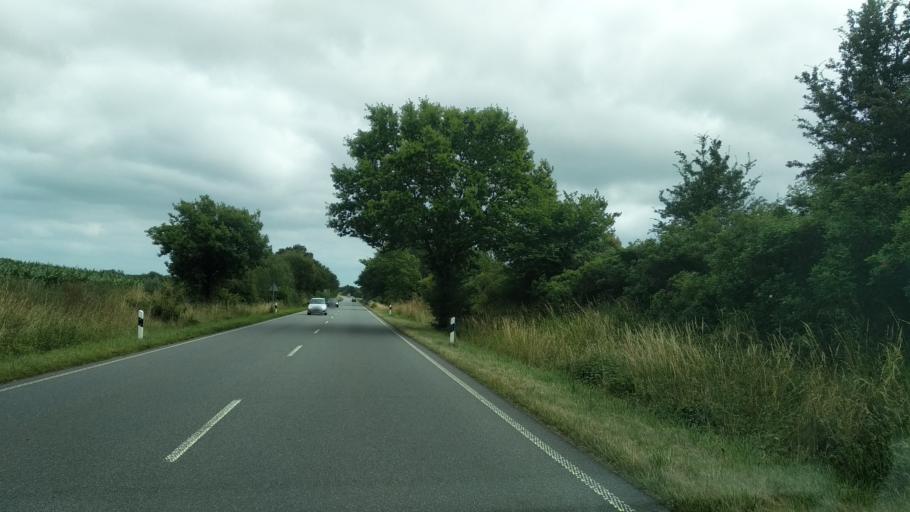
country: DE
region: Schleswig-Holstein
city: Neuberend
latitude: 54.5445
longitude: 9.5471
